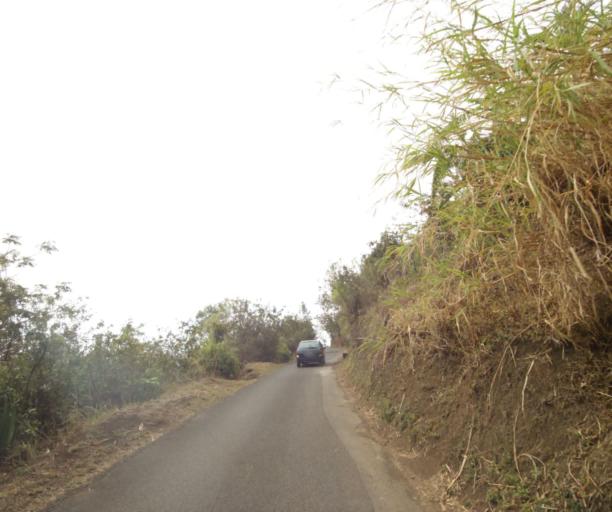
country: RE
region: Reunion
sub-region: Reunion
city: Saint-Paul
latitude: -21.0262
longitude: 55.3052
